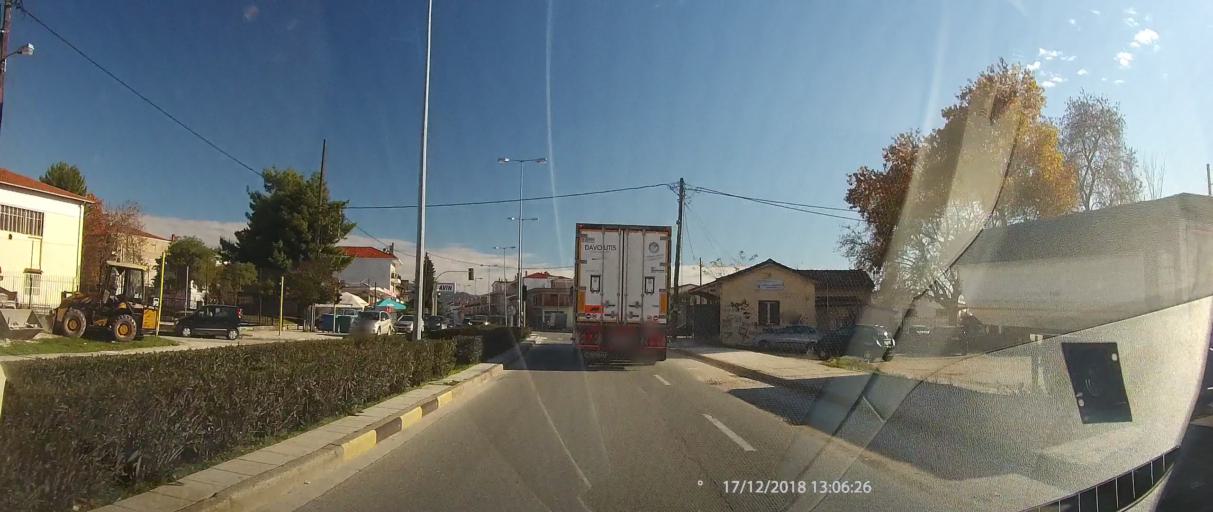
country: GR
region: Thessaly
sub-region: Trikala
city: Kalampaka
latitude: 39.7027
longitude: 21.6266
